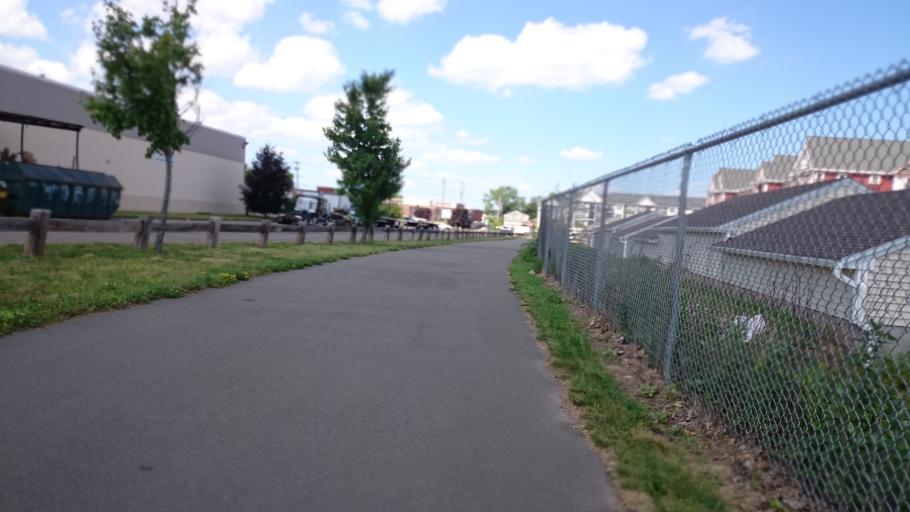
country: US
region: Connecticut
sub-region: New Haven County
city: New Haven
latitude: 41.3551
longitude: -72.9257
